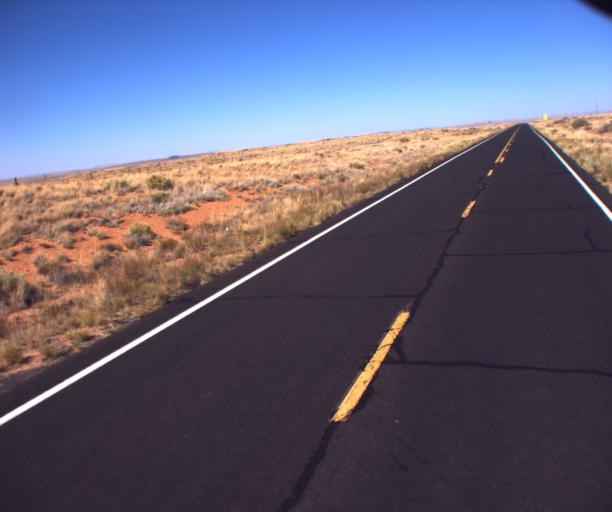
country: US
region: Arizona
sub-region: Navajo County
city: Dilkon
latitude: 35.5310
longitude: -110.4456
